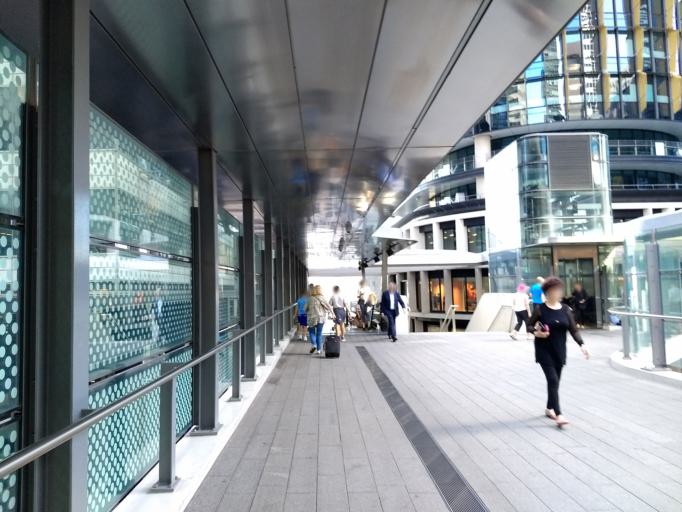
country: AU
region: New South Wales
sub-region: City of Sydney
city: Sydney
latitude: -33.8652
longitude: 151.2030
